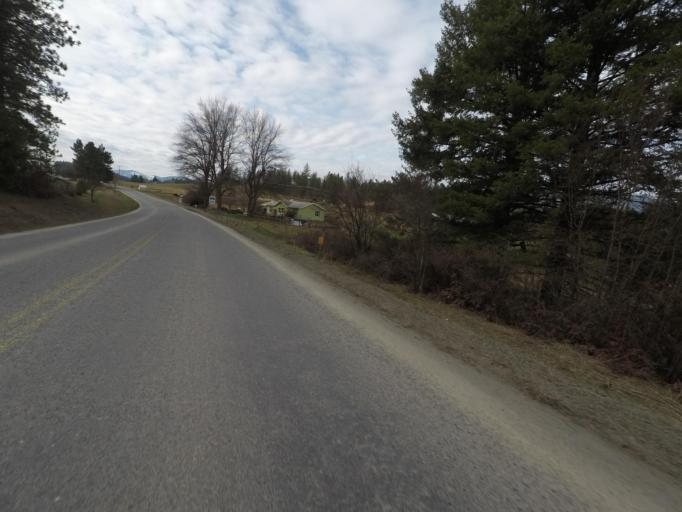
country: US
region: Washington
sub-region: Stevens County
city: Colville
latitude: 48.5280
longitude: -117.8801
